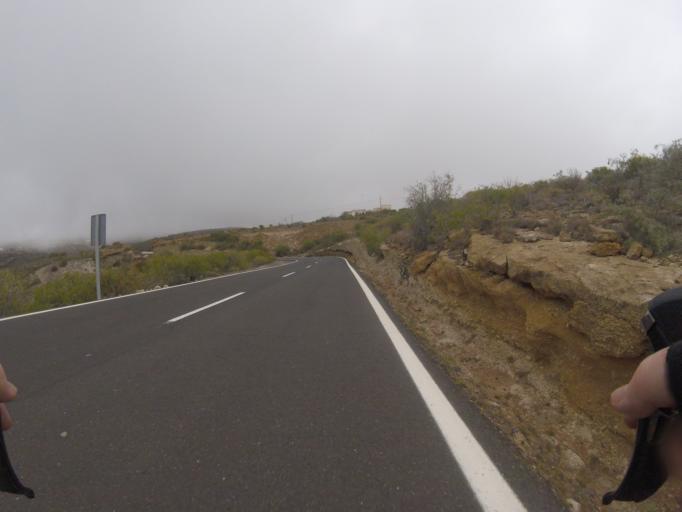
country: ES
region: Canary Islands
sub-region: Provincia de Santa Cruz de Tenerife
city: Lomo de Arico
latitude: 28.1985
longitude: -16.4618
